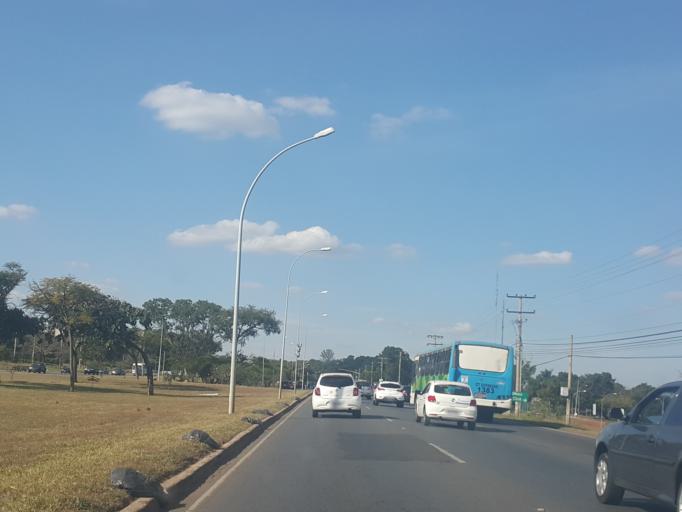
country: BR
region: Federal District
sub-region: Brasilia
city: Brasilia
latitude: -15.8092
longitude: -47.9348
